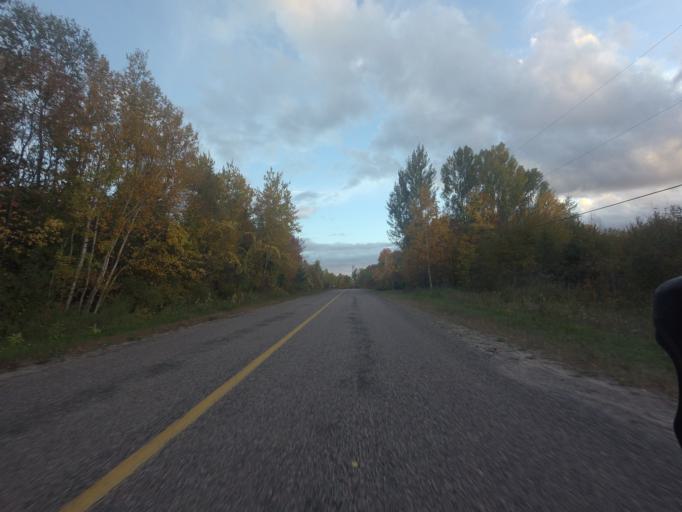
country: CA
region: Ontario
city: Renfrew
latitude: 45.4139
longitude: -76.9539
